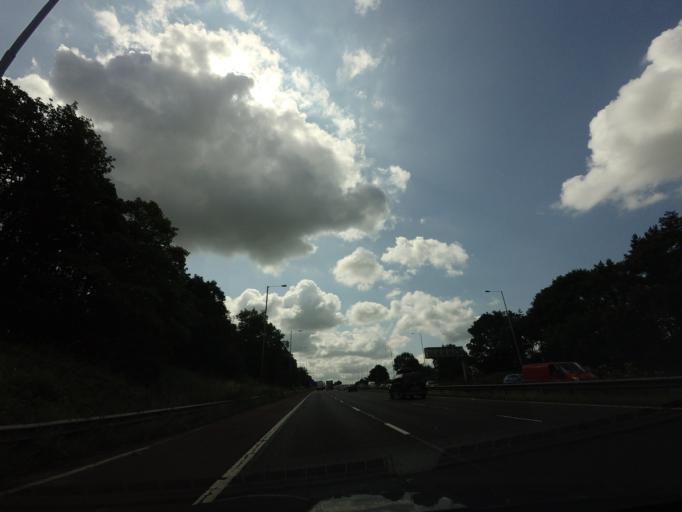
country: GB
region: England
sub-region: Lancashire
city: Euxton
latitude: 53.6509
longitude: -2.6910
